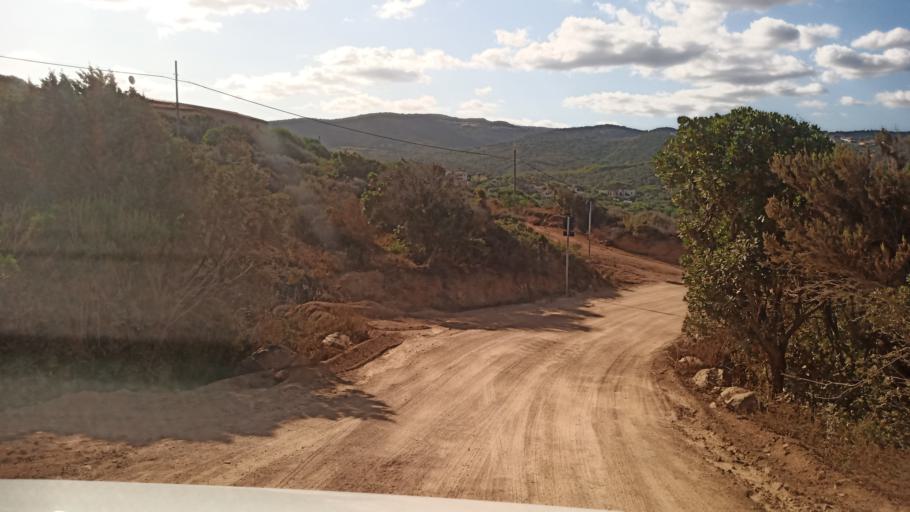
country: IT
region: Sardinia
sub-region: Provincia di Olbia-Tempio
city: Trinita d'Agultu
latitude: 41.0191
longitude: 8.8904
